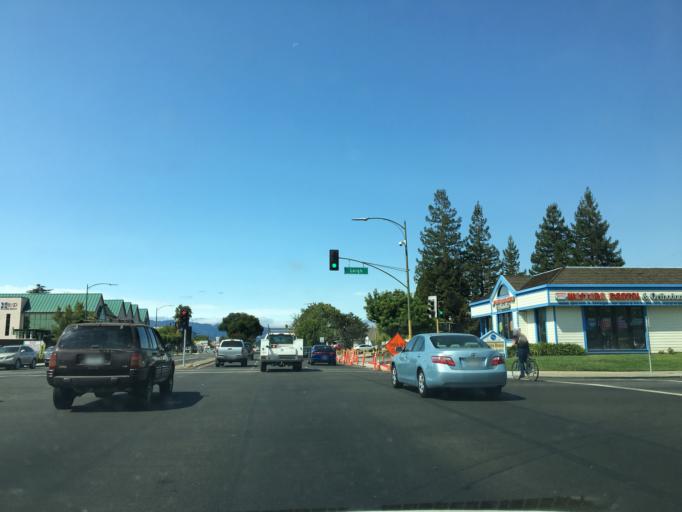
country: US
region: California
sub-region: Santa Clara County
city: Cambrian Park
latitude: 37.2618
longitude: -121.9221
